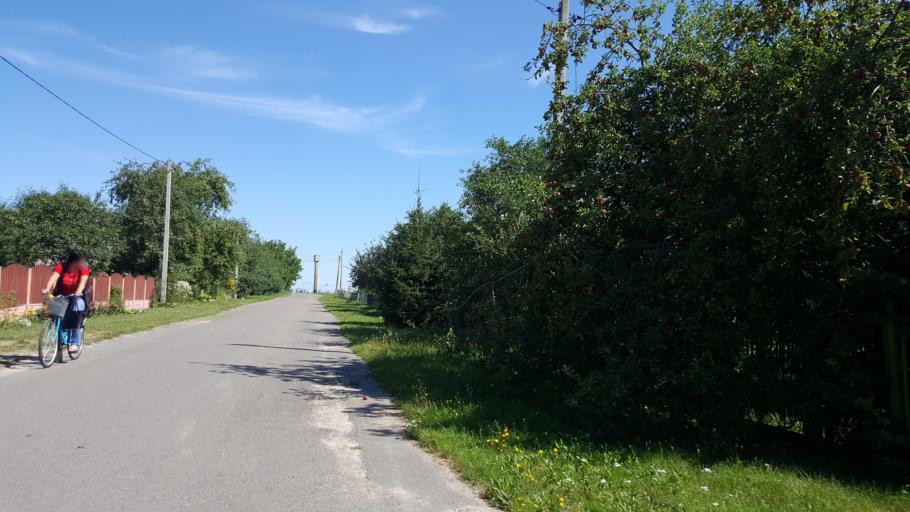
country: BY
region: Brest
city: Charnawchytsy
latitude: 52.2760
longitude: 23.7666
